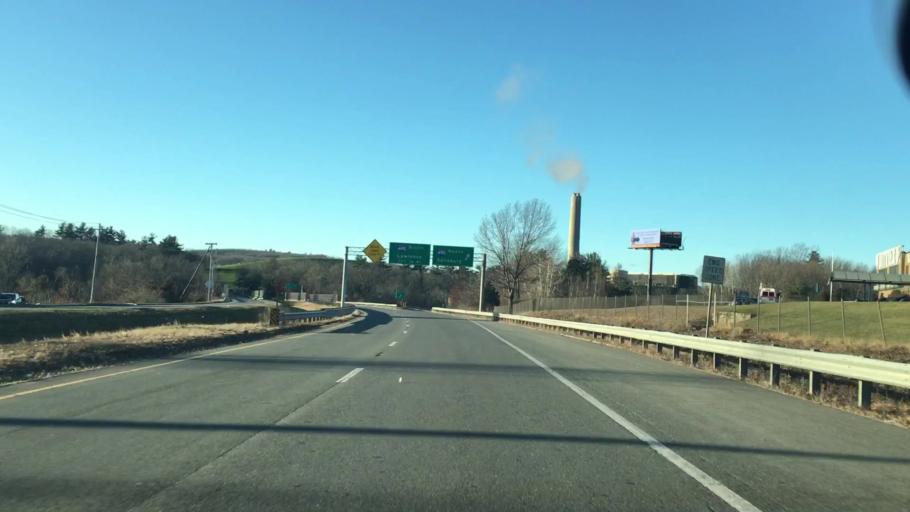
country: US
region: Massachusetts
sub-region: Essex County
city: Haverhill
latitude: 42.7604
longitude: -71.1188
